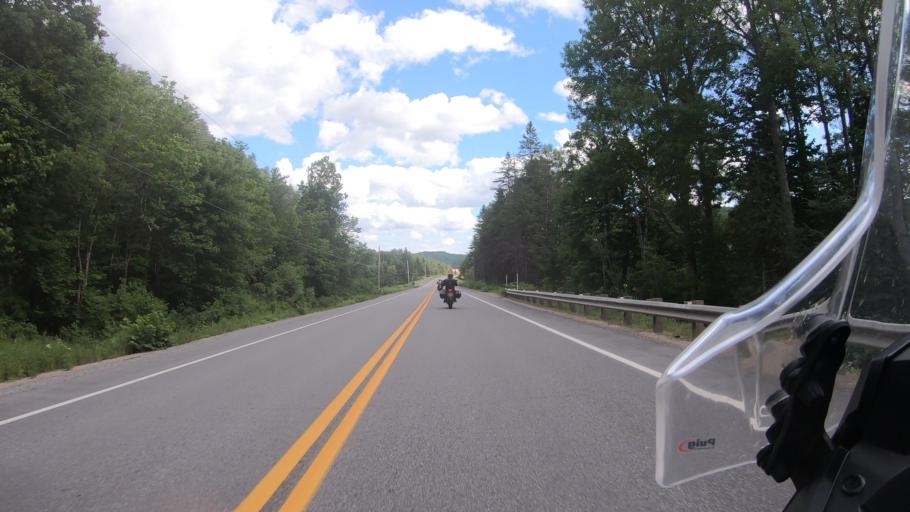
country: CA
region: Quebec
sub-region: Mauricie
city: Saint-Tite
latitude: 46.9904
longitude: -72.9135
